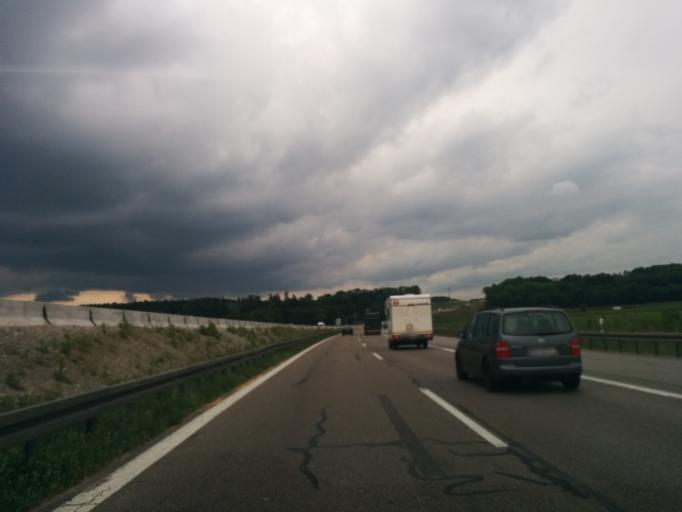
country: DE
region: Bavaria
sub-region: Swabia
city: Burgau
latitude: 48.4126
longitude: 10.4177
